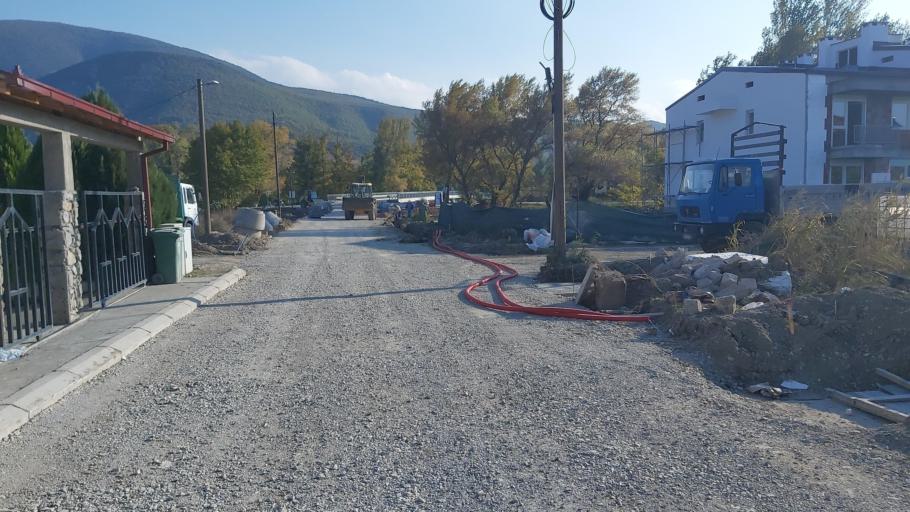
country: MK
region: Demir Kapija
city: Demir Kapija
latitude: 41.4076
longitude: 22.2426
